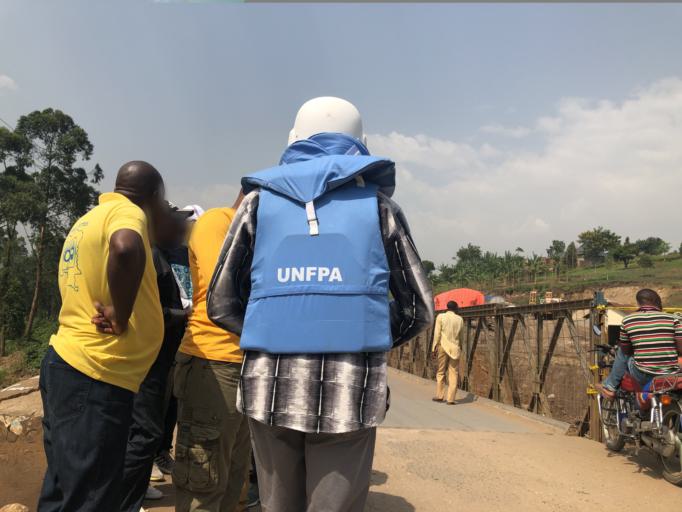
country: UG
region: Western Region
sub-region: Kasese District
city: Kilembe
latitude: 0.0411
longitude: 29.7200
